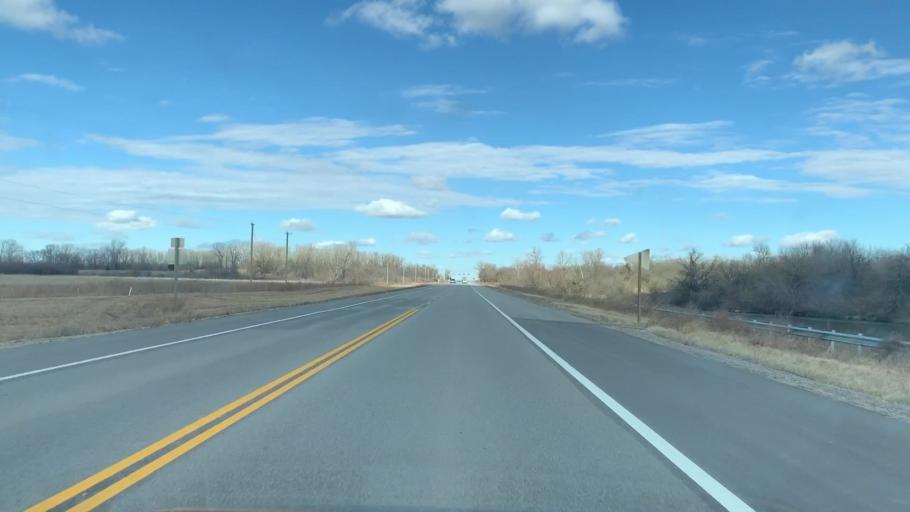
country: US
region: Kansas
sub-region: Cherokee County
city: Columbus
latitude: 37.3159
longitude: -94.8323
